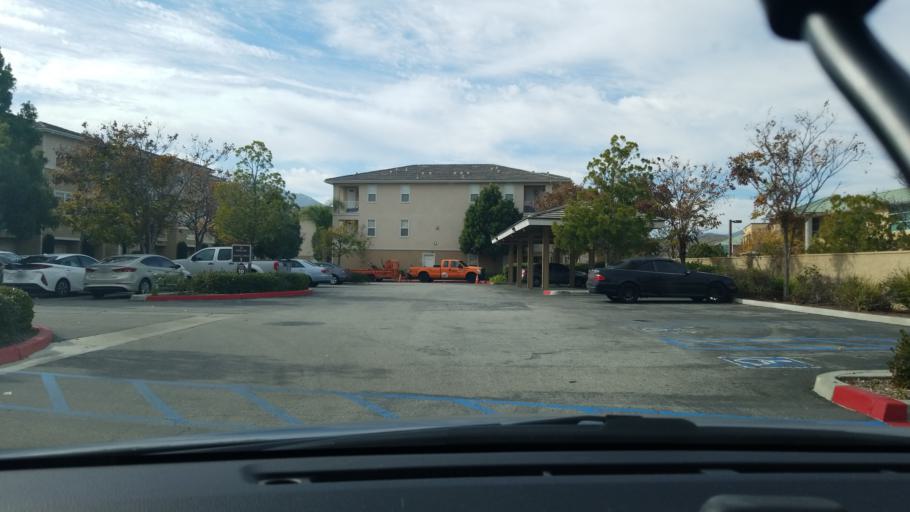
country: US
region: California
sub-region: Riverside County
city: Temecula
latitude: 33.4754
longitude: -117.1157
